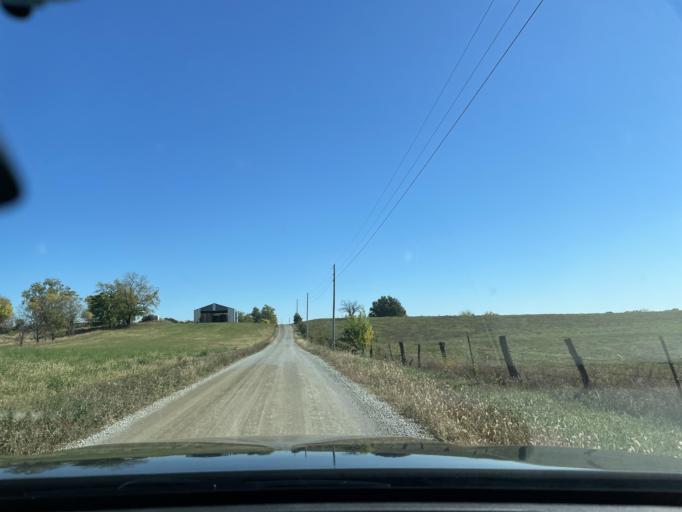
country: US
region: Missouri
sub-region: Andrew County
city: Savannah
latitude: 39.9392
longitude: -94.8785
